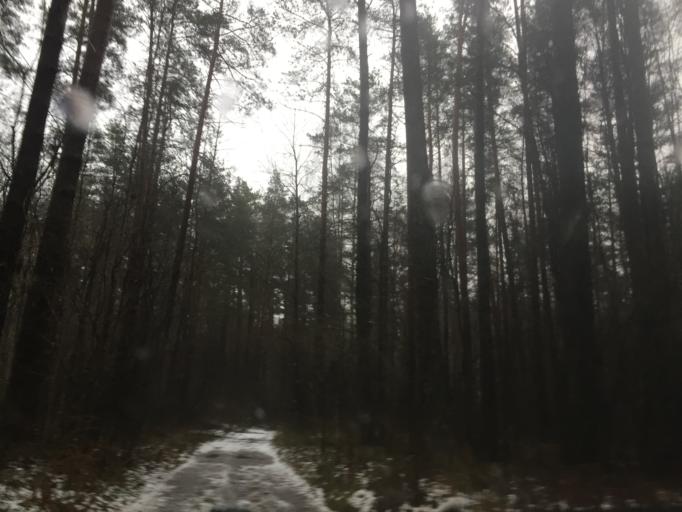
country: LV
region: Stopini
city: Ulbroka
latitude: 56.9528
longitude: 24.3379
